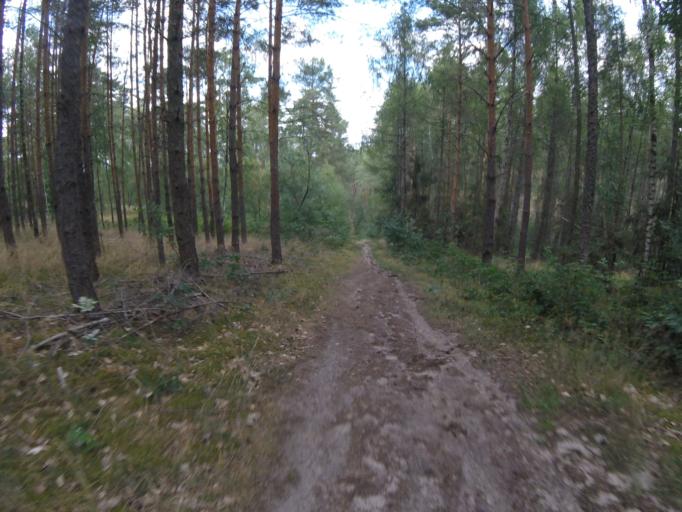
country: DE
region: Brandenburg
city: Schlepzig
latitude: 52.0583
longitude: 13.8012
